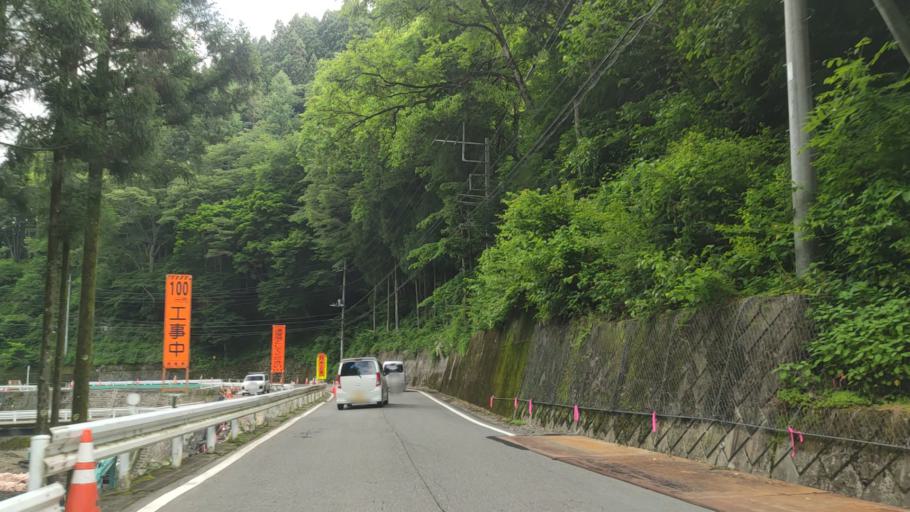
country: JP
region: Gunma
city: Tomioka
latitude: 36.1057
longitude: 138.7172
